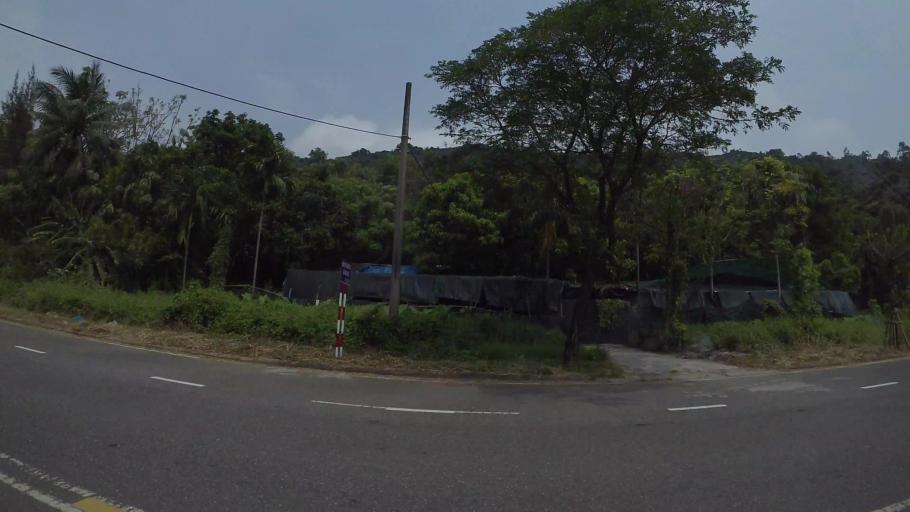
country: VN
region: Da Nang
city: Son Tra
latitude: 16.1067
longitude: 108.2632
